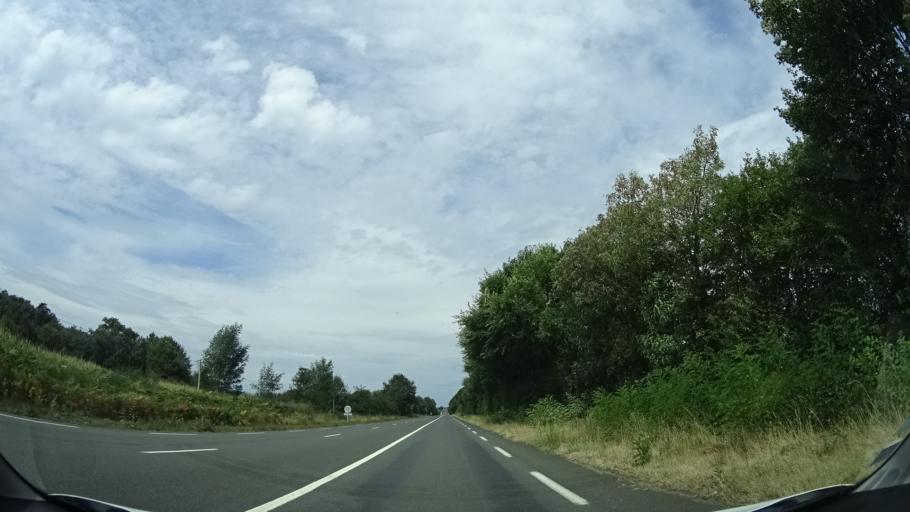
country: FR
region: Pays de la Loire
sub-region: Departement de la Sarthe
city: Vion
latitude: 47.7681
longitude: -0.1976
